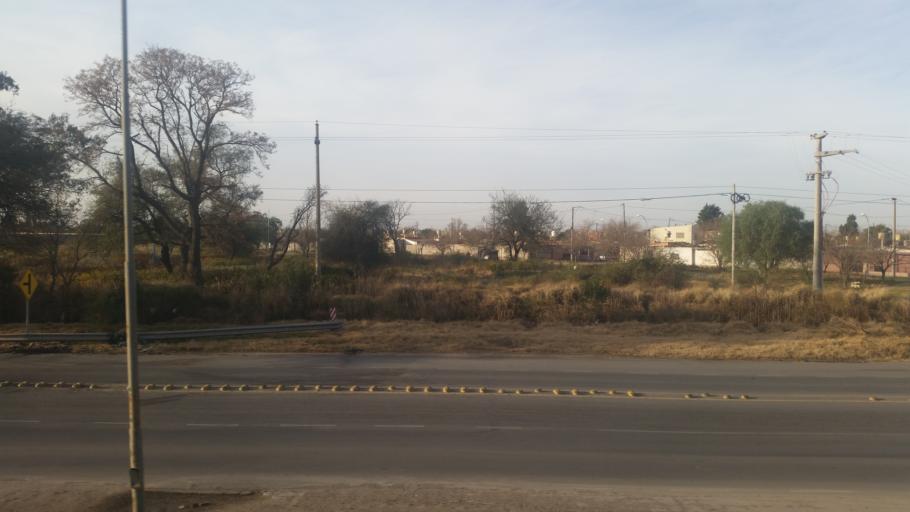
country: AR
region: Cordoba
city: Malvinas Argentinas
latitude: -31.4771
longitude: -64.0908
